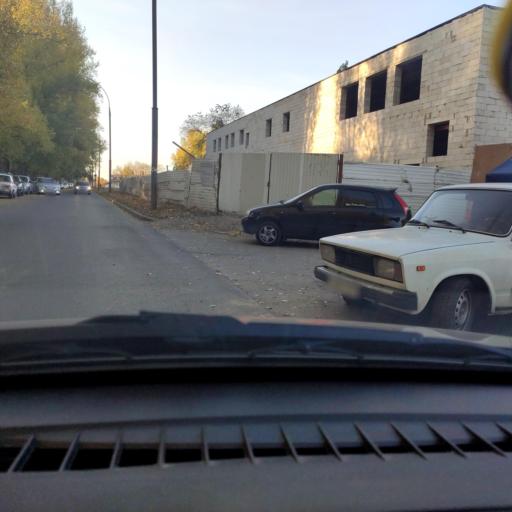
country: RU
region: Samara
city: Tol'yatti
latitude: 53.5259
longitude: 49.2818
